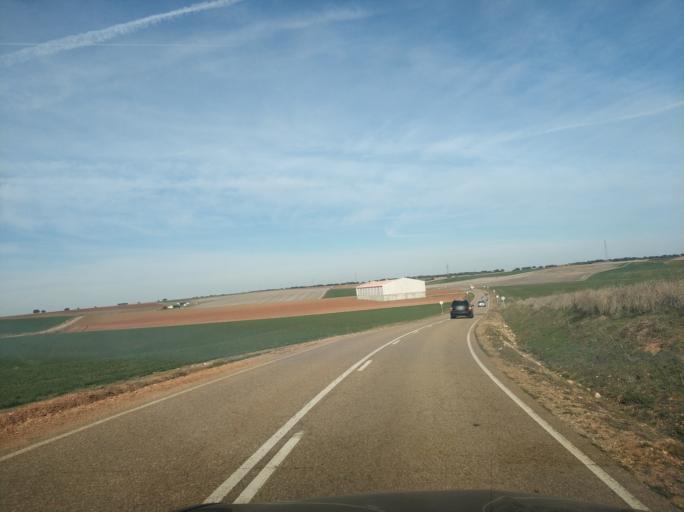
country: ES
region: Castille and Leon
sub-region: Provincia de Salamanca
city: Parada de Arriba
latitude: 40.9877
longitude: -5.7993
